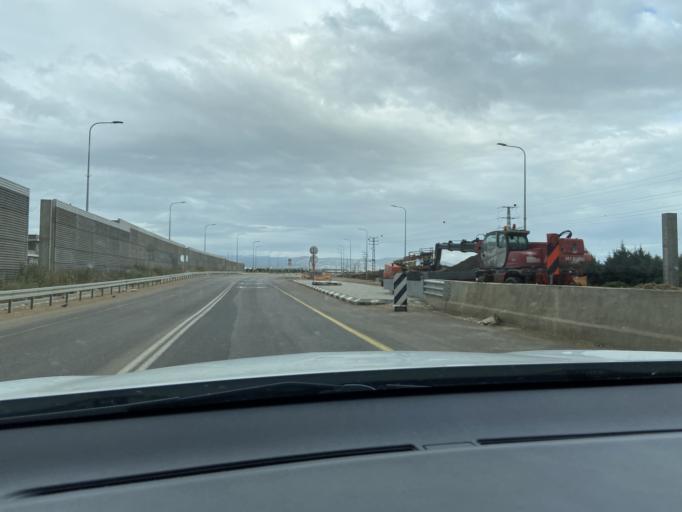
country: IL
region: Northern District
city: El Mazra`a
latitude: 32.9801
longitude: 35.1038
